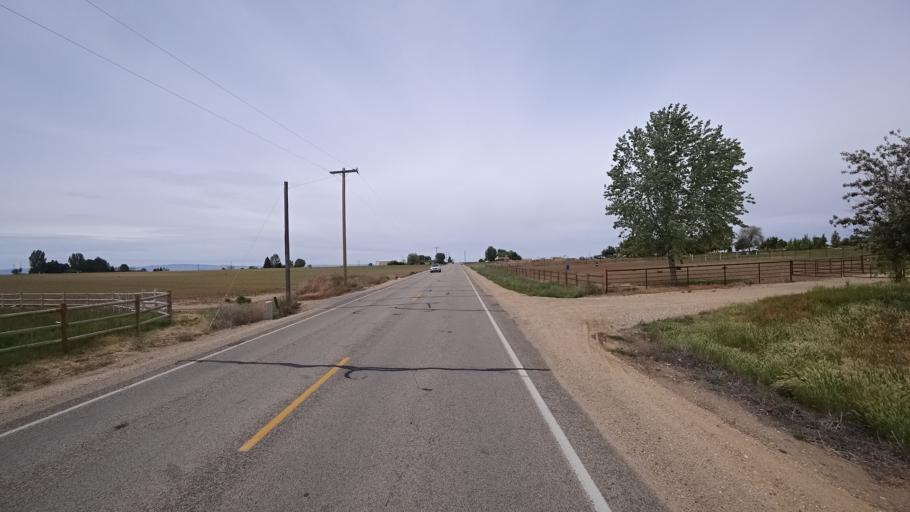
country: US
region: Idaho
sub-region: Ada County
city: Meridian
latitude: 43.5610
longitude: -116.4239
